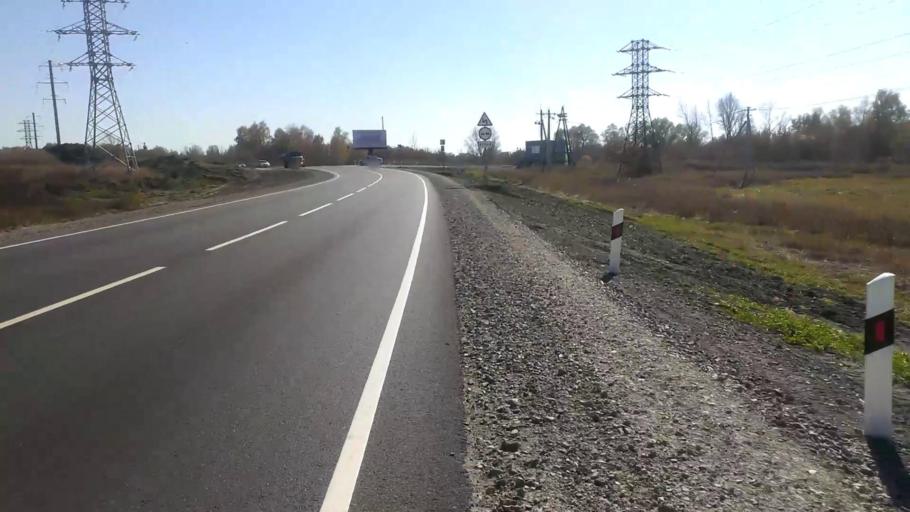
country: RU
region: Altai Krai
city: Sannikovo
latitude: 53.3302
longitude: 83.9386
